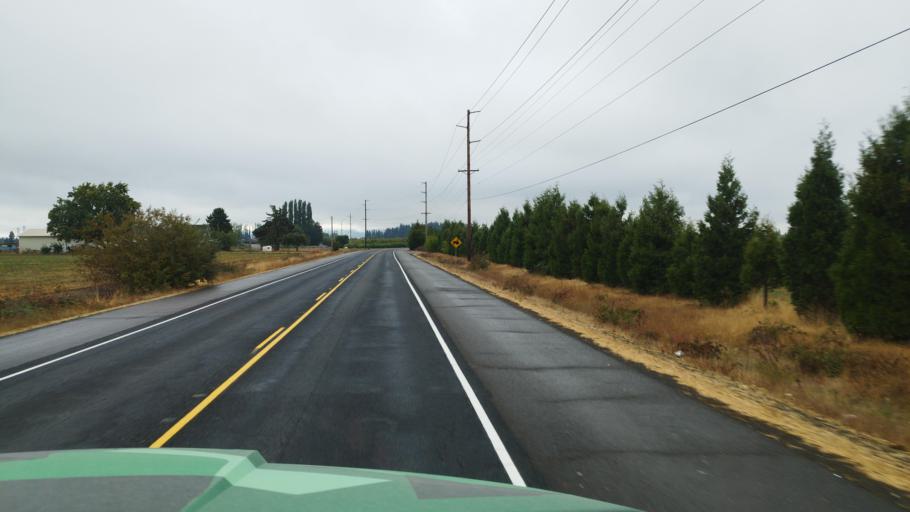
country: US
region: Oregon
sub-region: Washington County
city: Cornelius
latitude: 45.5436
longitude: -123.0734
